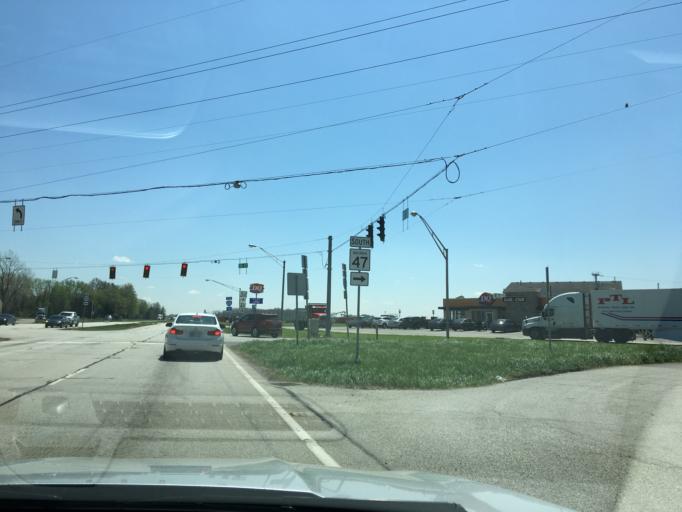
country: US
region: Indiana
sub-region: Boone County
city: Thorntown
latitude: 40.1271
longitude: -86.5619
